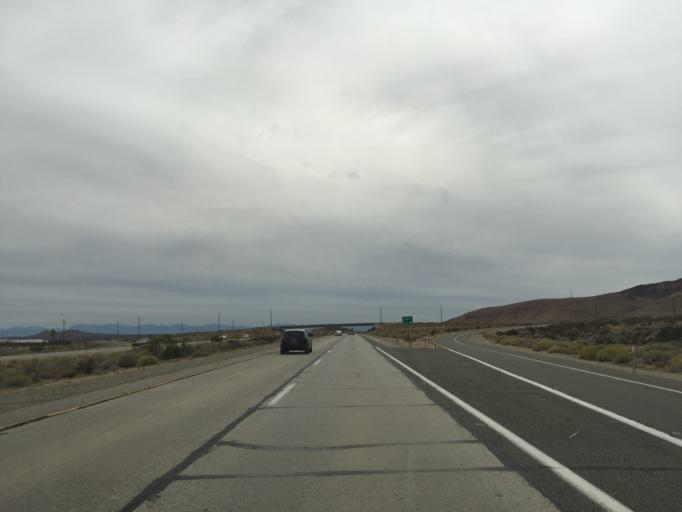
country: US
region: California
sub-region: Kern County
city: Mojave
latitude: 34.9996
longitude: -118.1601
